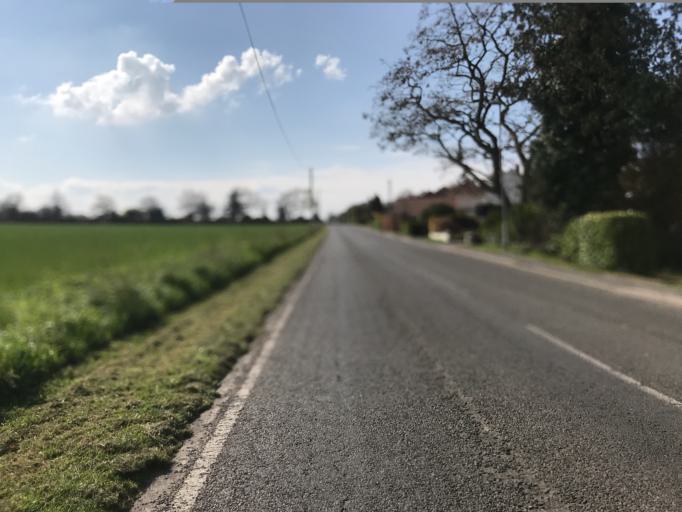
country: GB
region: England
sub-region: Cambridgeshire
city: Sawston
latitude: 52.1621
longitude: 0.1584
